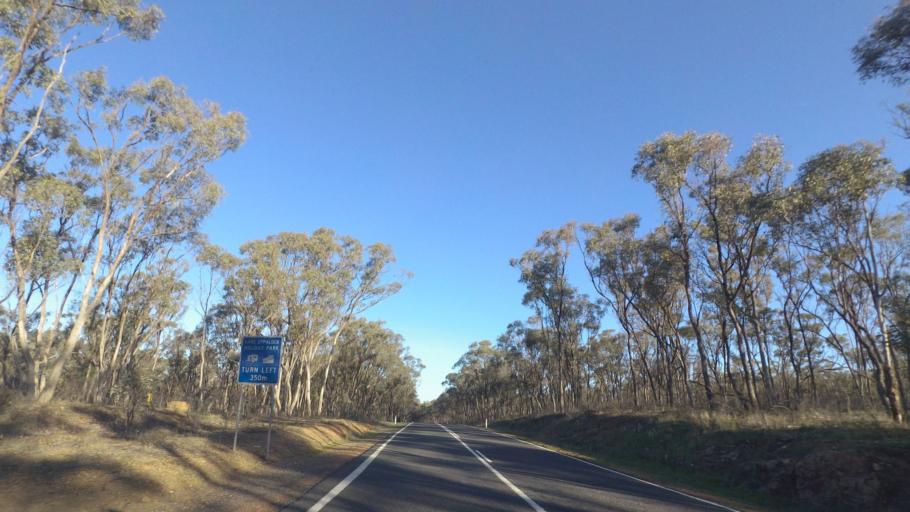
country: AU
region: Victoria
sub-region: Greater Bendigo
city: Kennington
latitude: -36.8883
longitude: 144.4931
